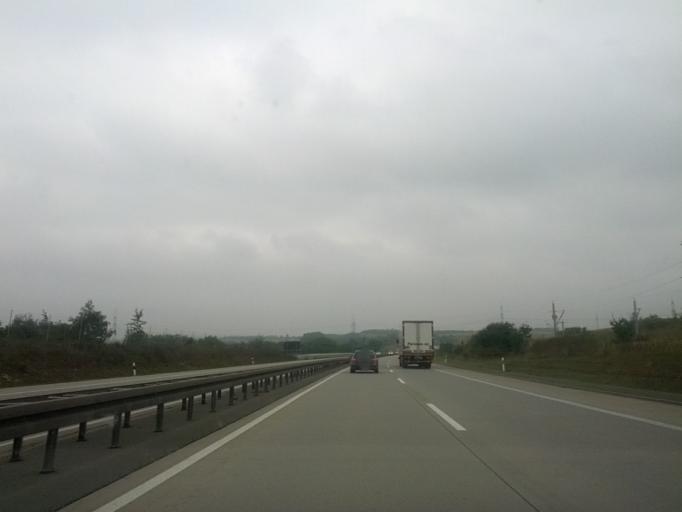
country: DE
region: Thuringia
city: Ingersleben
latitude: 50.9201
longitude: 10.9461
